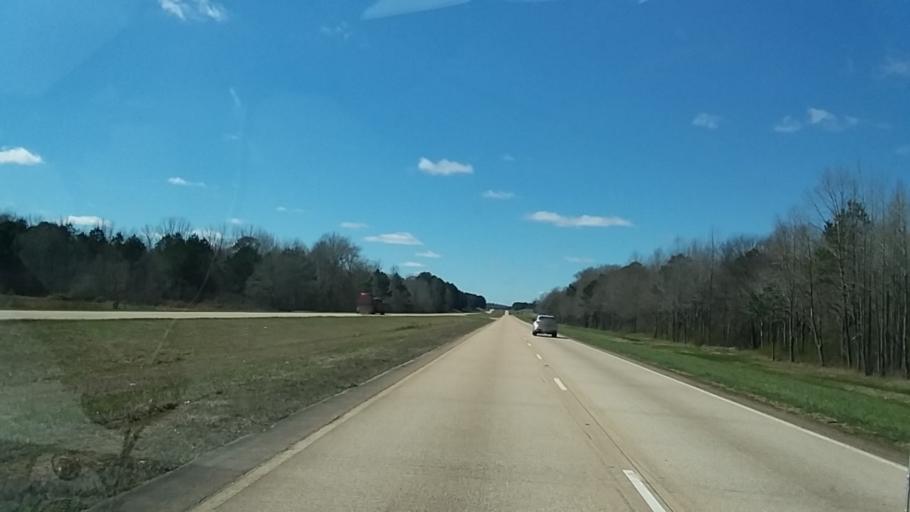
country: US
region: Mississippi
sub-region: Tishomingo County
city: Iuka
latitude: 34.8049
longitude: -88.2469
